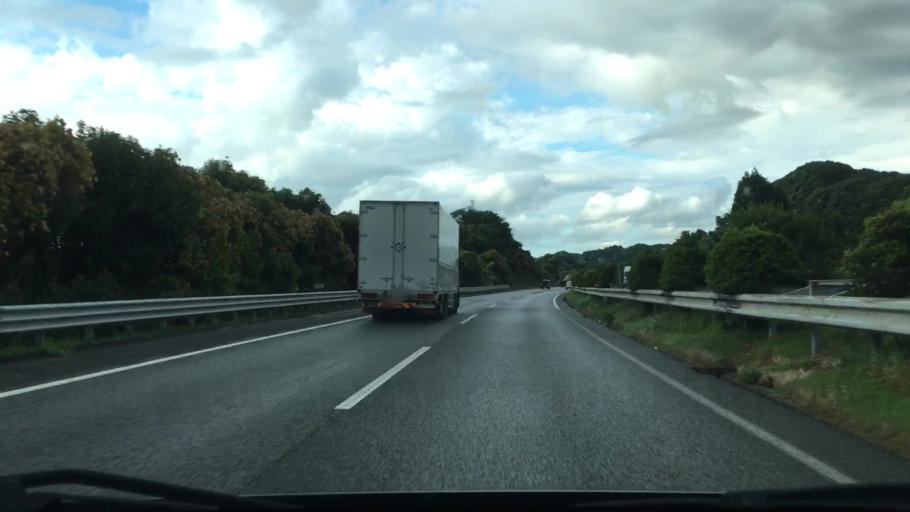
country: JP
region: Fukuoka
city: Koga
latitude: 33.7030
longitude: 130.4850
